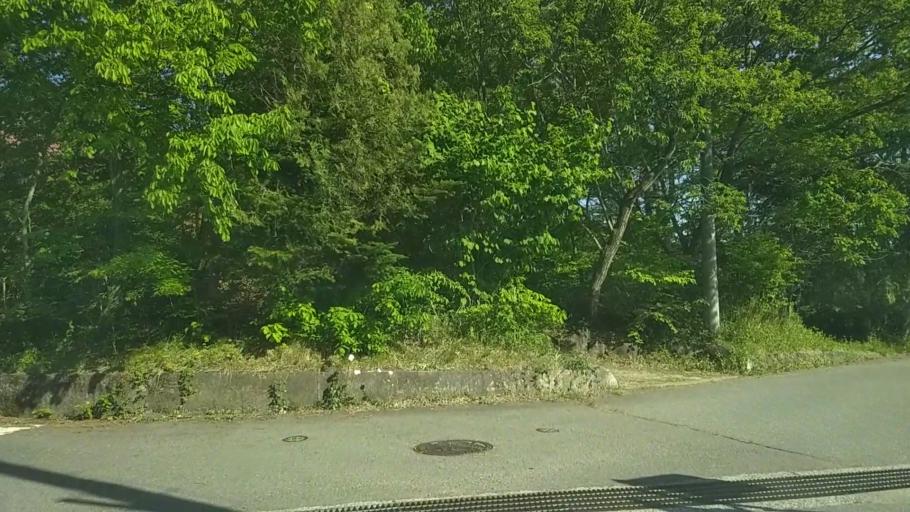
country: JP
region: Yamanashi
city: Nirasaki
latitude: 35.8761
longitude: 138.3603
